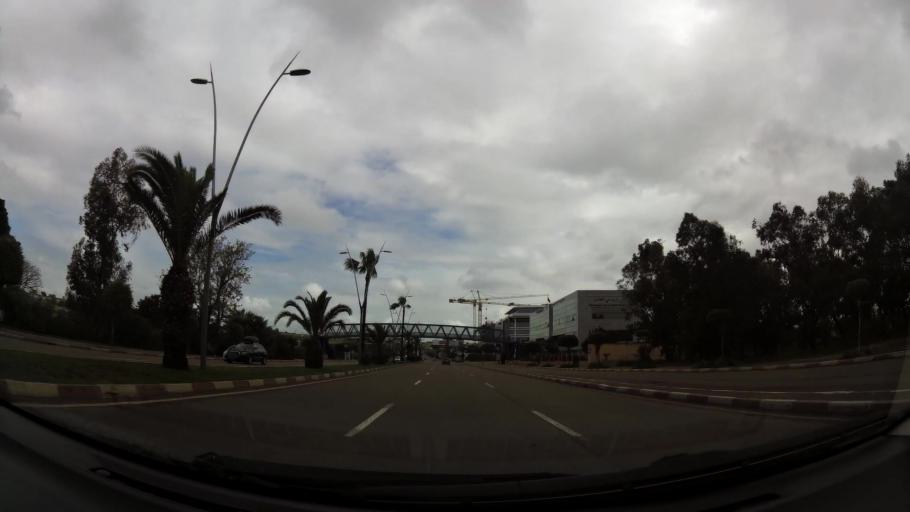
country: MA
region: Grand Casablanca
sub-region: Casablanca
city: Casablanca
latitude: 33.5239
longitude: -7.6351
